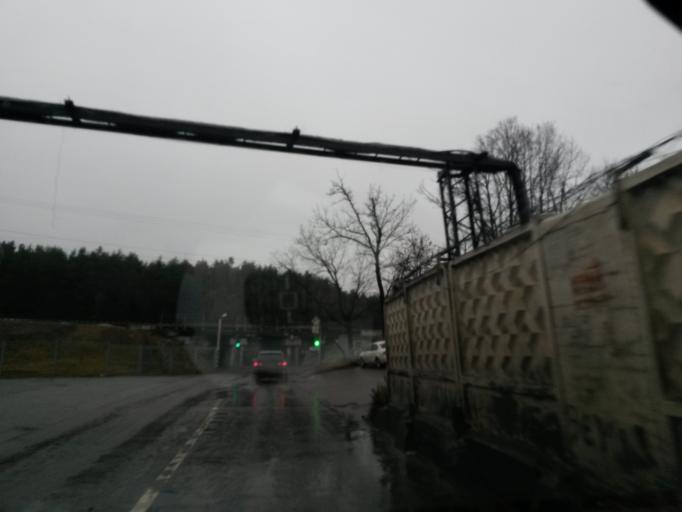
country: RU
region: Moskovskaya
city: Zarech'ye
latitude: 55.6617
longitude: 37.4085
